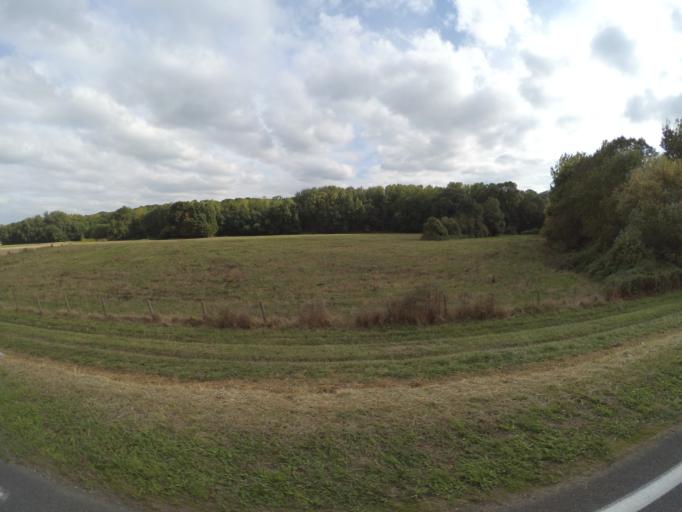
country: FR
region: Centre
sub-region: Departement d'Indre-et-Loire
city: Vernou-sur-Brenne
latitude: 47.4297
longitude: 0.8500
